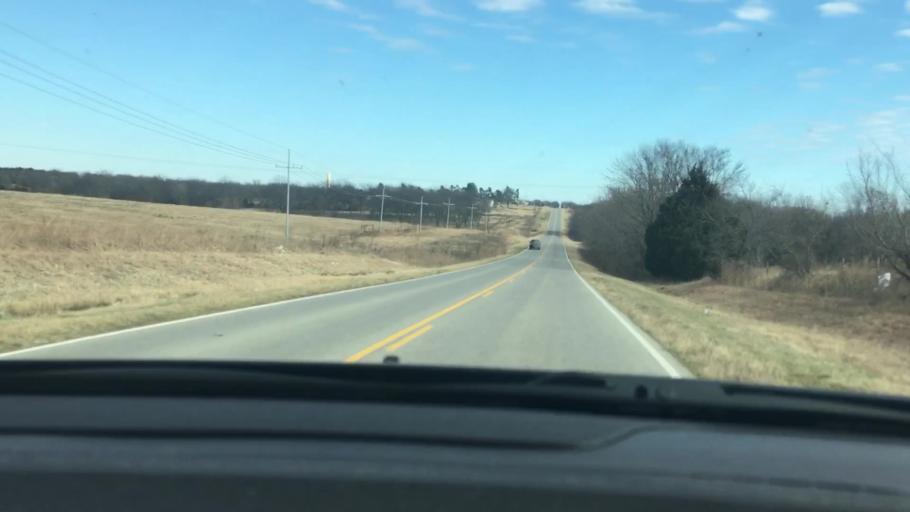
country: US
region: Oklahoma
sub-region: Garvin County
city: Stratford
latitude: 34.7968
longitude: -96.8293
